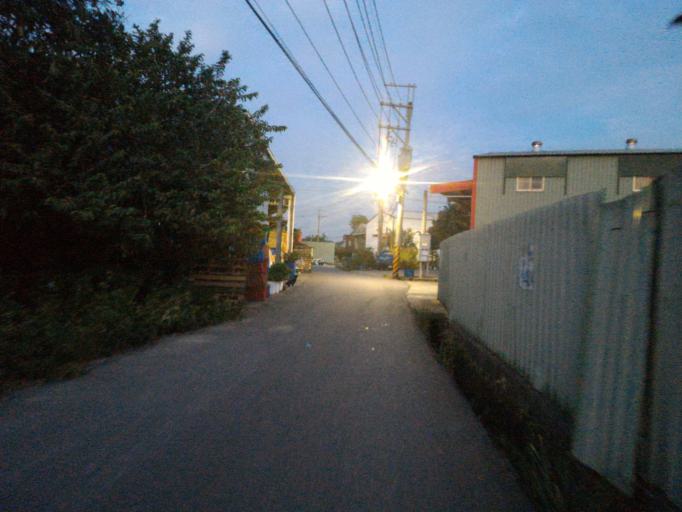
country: TW
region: Taipei
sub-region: Taipei
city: Banqiao
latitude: 24.9630
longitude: 121.4034
